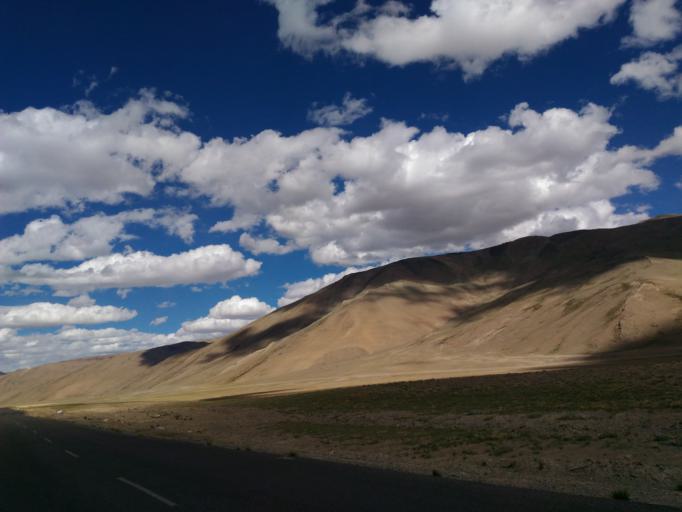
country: IN
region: Kashmir
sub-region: Kargil
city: Padam
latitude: 33.2354
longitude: 77.8121
